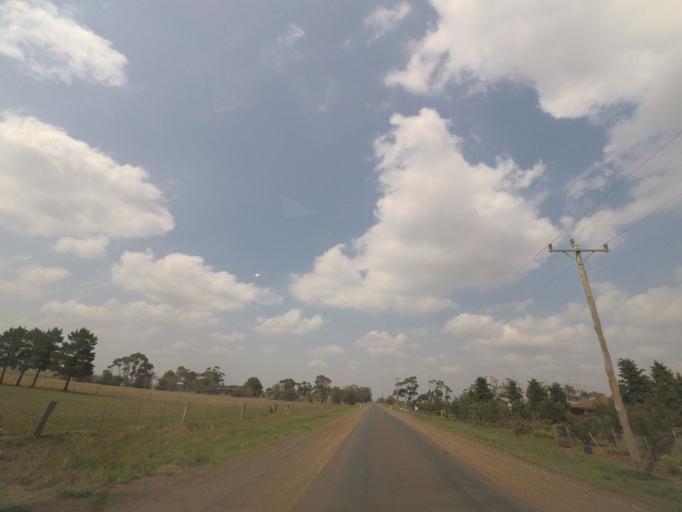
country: AU
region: Victoria
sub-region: Melton
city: Melton West
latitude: -37.6537
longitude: 144.5557
